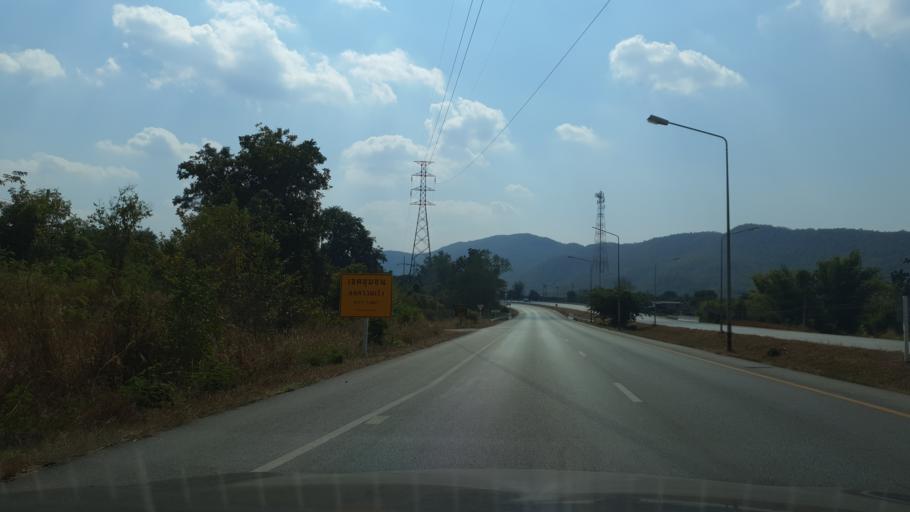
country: TH
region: Lampang
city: Mae Phrik
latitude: 17.3668
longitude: 99.1475
